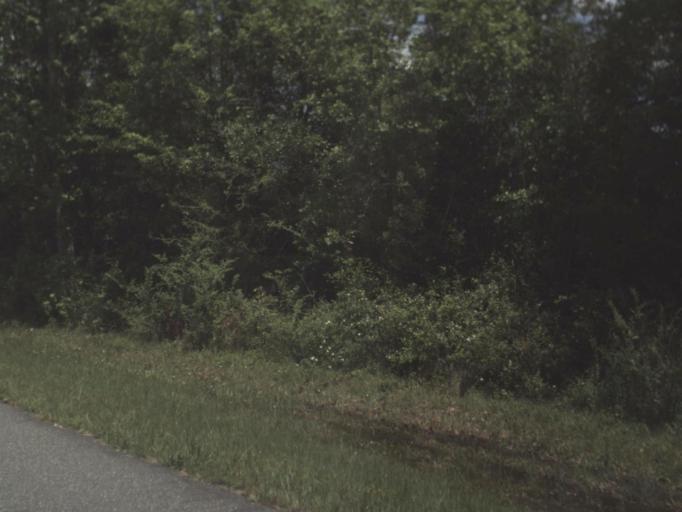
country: US
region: Florida
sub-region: Santa Rosa County
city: Point Baker
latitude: 30.7379
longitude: -87.0432
